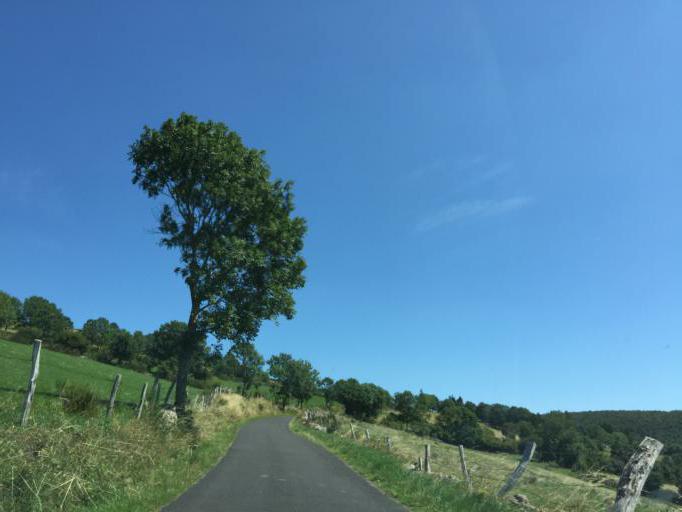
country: FR
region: Midi-Pyrenees
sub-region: Departement de l'Aveyron
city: Laguiole
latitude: 44.6546
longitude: 2.8954
